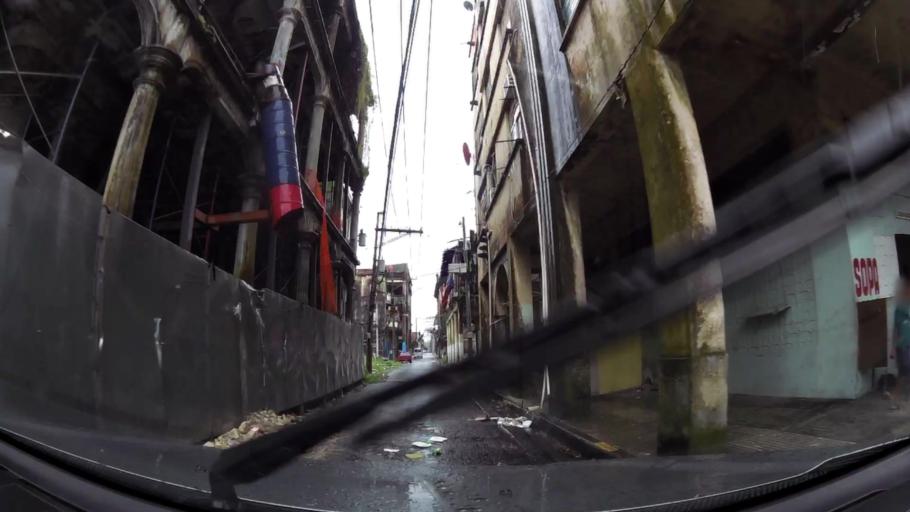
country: PA
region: Colon
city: Colon
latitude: 9.3608
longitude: -79.9053
